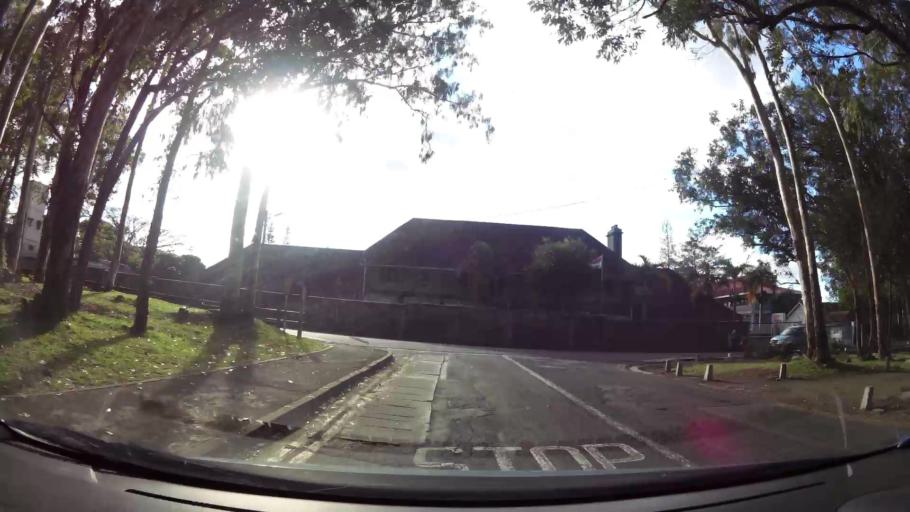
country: MU
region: Plaines Wilhems
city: Vacoas
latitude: -20.2943
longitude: 57.4967
